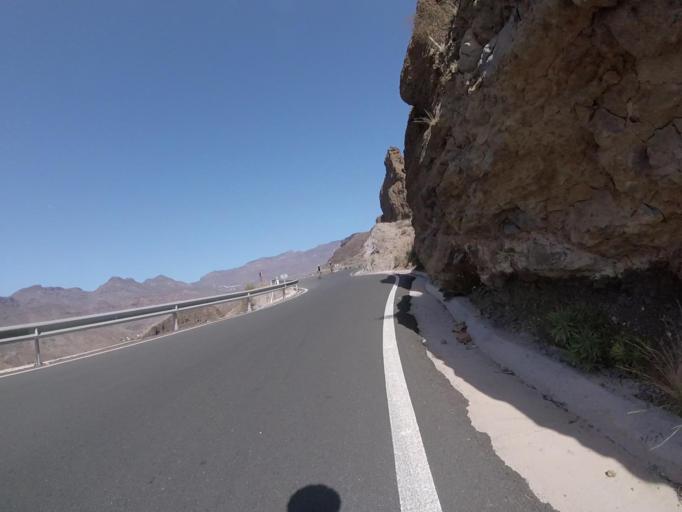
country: ES
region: Canary Islands
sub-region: Provincia de Las Palmas
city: Santa Lucia
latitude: 27.8828
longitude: -15.5228
